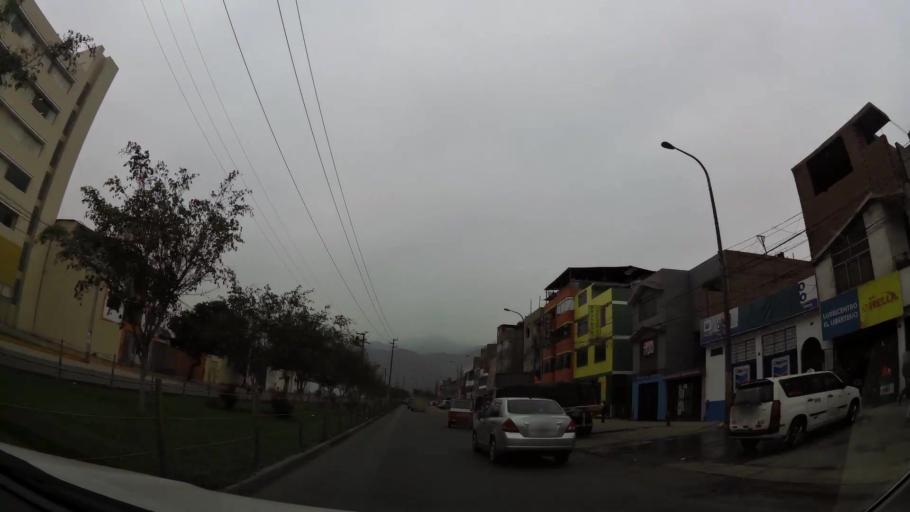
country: PE
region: Lima
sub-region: Lima
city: Independencia
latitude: -11.9853
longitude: -77.0052
